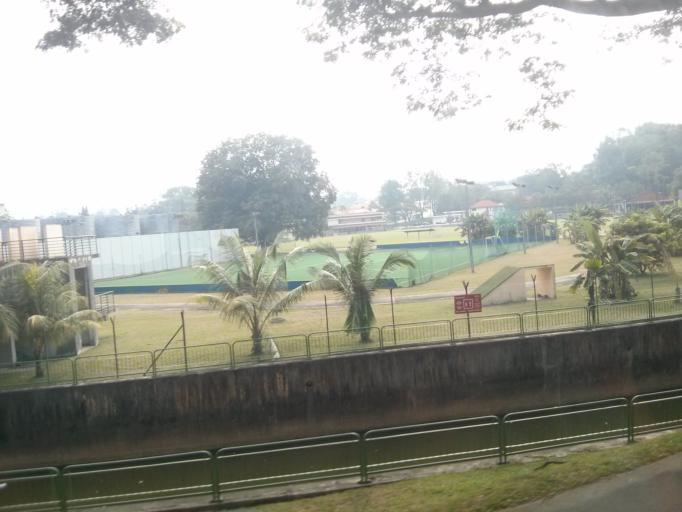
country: SG
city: Singapore
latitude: 1.3301
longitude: 103.8394
